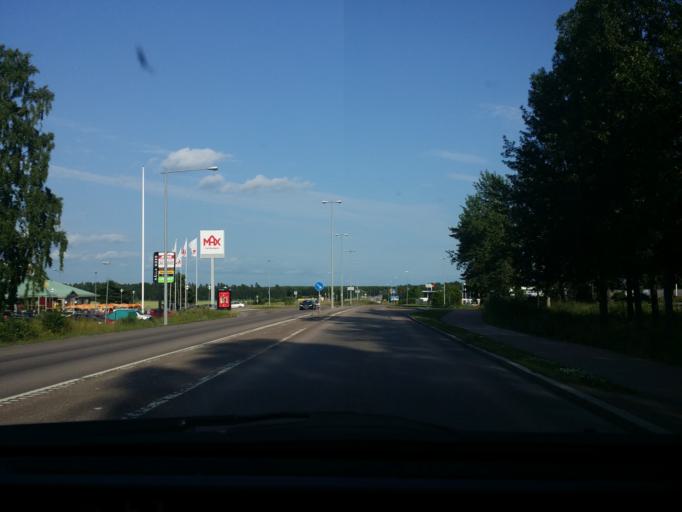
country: SE
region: Vaestmanland
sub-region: Vasteras
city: Vasteras
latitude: 59.6126
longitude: 16.6117
